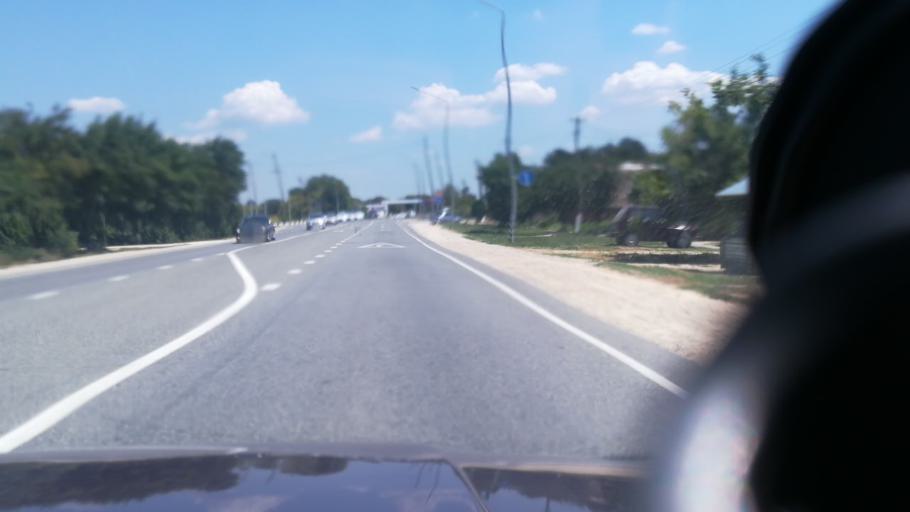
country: RU
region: Krasnodarskiy
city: Vinogradnyy
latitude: 45.0558
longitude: 37.3243
